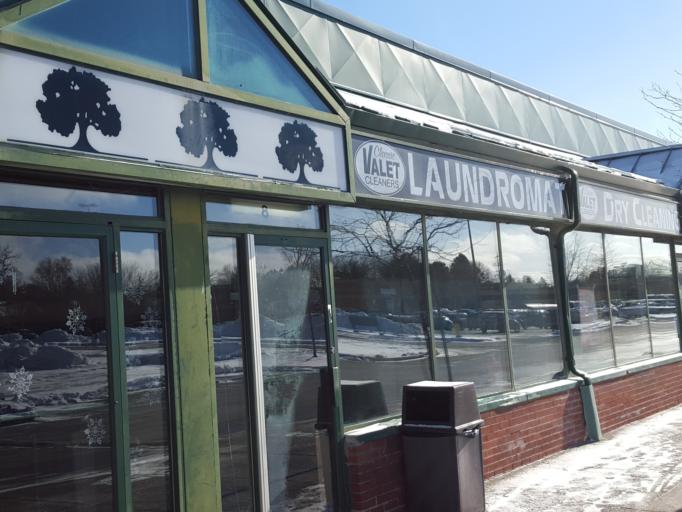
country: CA
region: Ontario
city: Keswick
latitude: 44.2149
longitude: -79.4630
